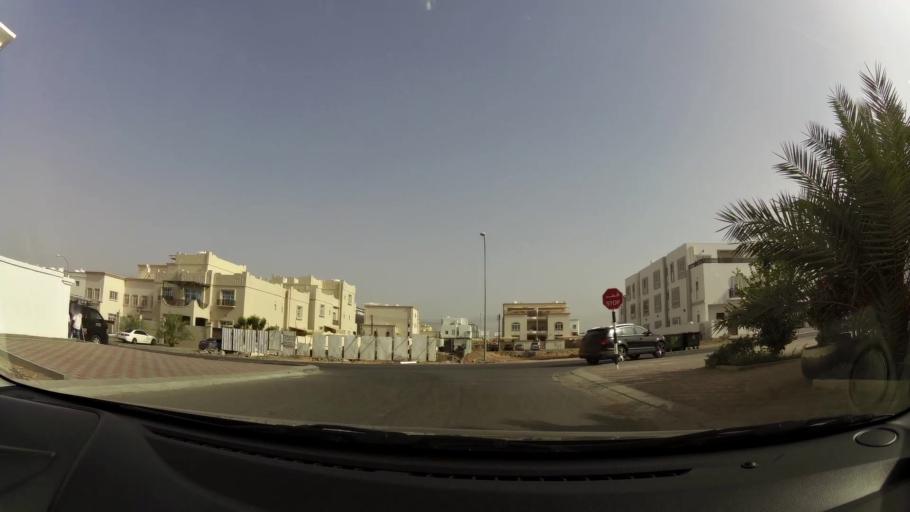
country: OM
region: Muhafazat Masqat
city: Bawshar
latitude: 23.5547
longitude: 58.3532
